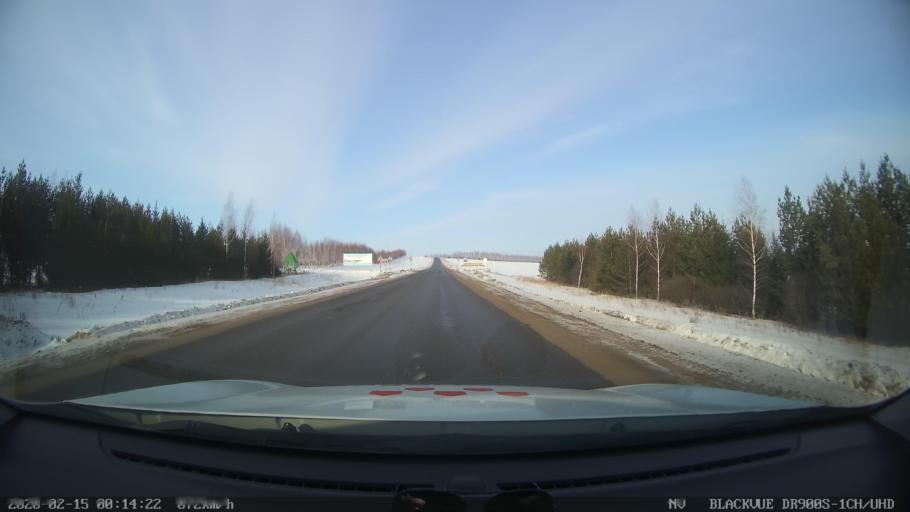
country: RU
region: Tatarstan
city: Stolbishchi
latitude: 55.4852
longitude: 49.0044
